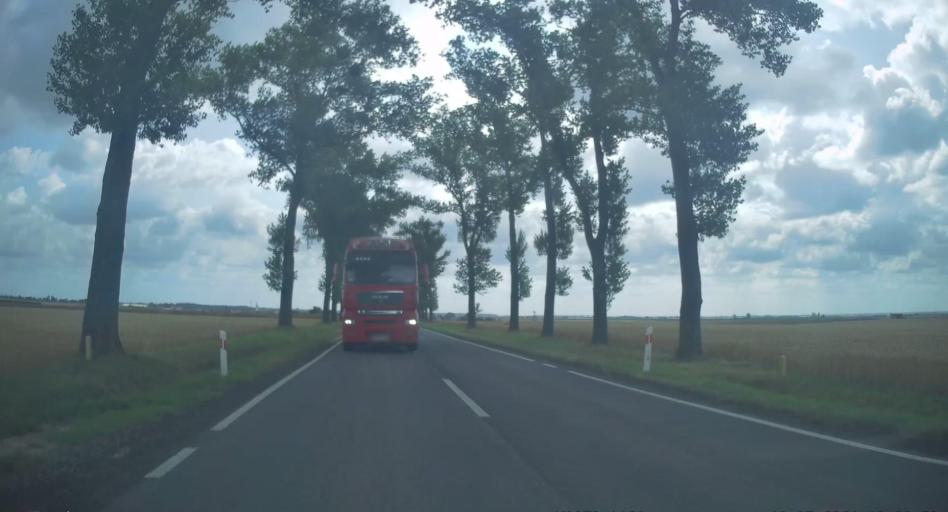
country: PL
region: Opole Voivodeship
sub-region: Powiat prudnicki
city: Glogowek
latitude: 50.3381
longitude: 17.9213
